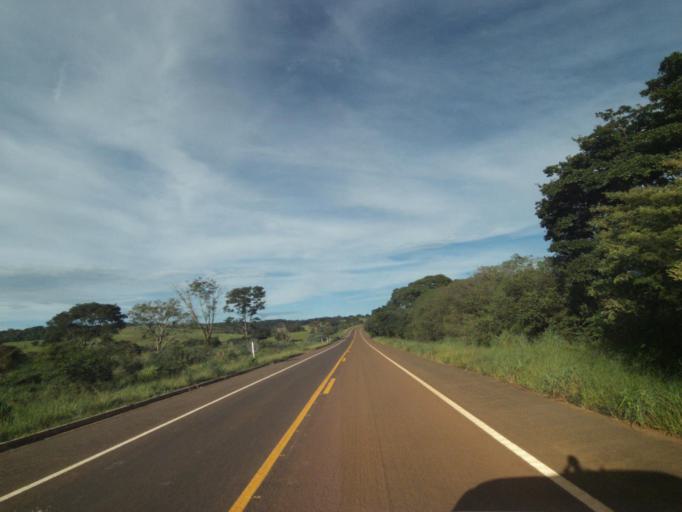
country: BR
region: Goias
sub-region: Jaragua
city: Jaragua
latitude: -15.8948
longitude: -49.5203
